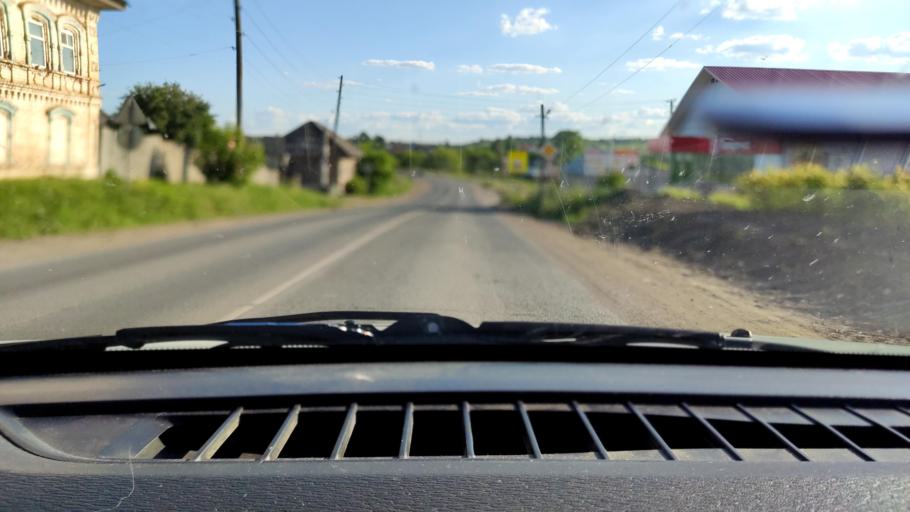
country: RU
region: Perm
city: Orda
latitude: 57.1957
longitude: 56.9058
